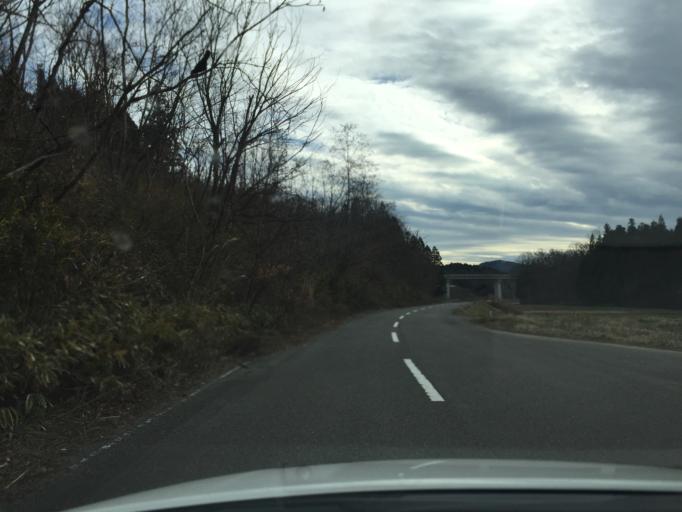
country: JP
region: Fukushima
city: Funehikimachi-funehiki
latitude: 37.2964
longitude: 140.6052
